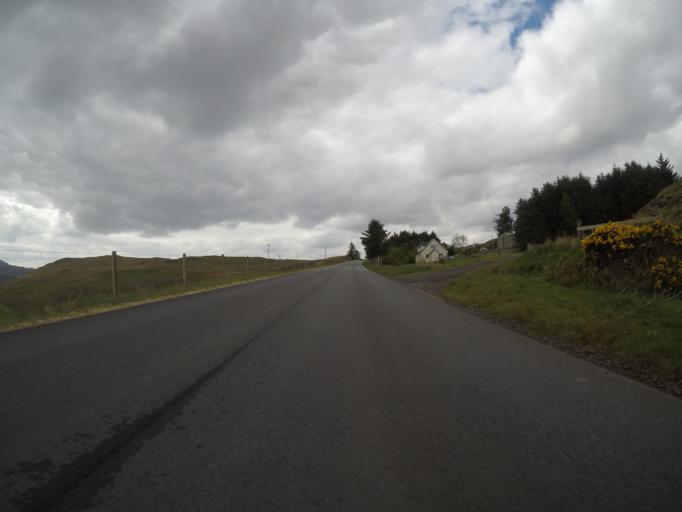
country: GB
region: Scotland
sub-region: Highland
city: Isle of Skye
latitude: 57.3309
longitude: -6.3412
